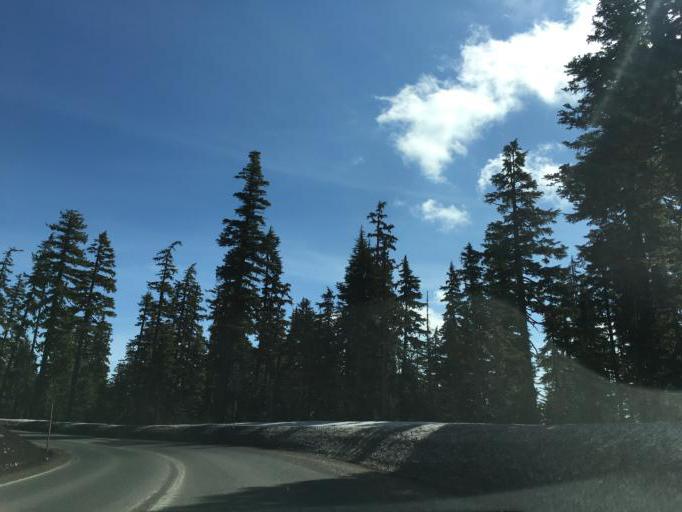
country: US
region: Oregon
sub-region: Clackamas County
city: Mount Hood Village
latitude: 45.3045
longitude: -121.7190
